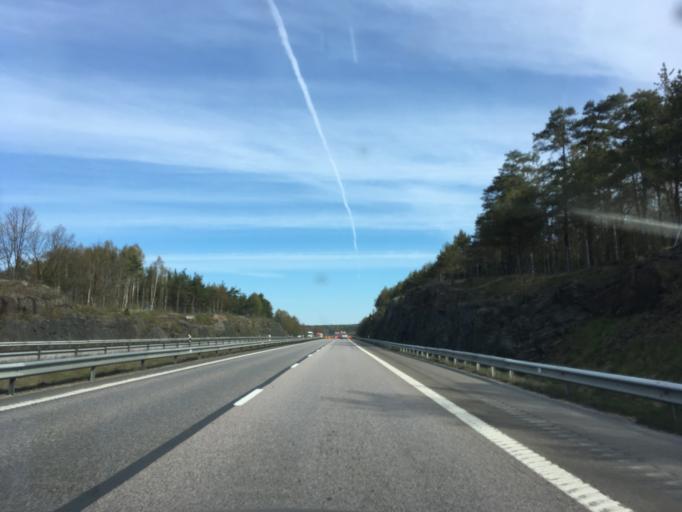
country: SE
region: Halland
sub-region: Varbergs Kommun
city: Veddige
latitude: 57.2113
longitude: 12.2413
